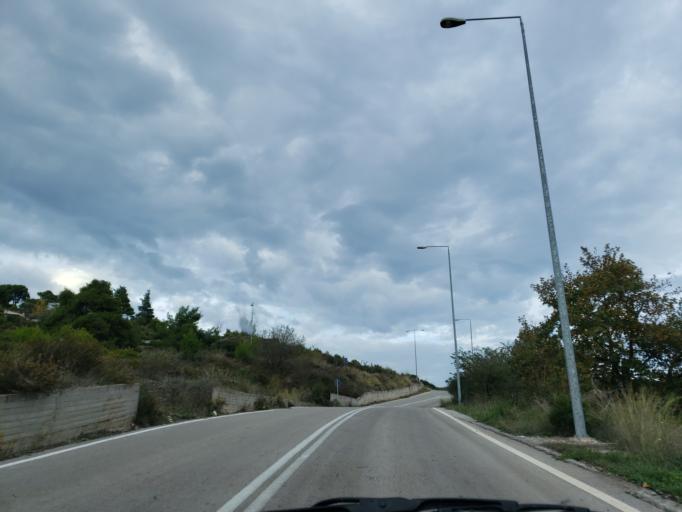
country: GR
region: Attica
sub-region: Nomarchia Anatolikis Attikis
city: Varnavas
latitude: 38.2206
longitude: 23.9273
